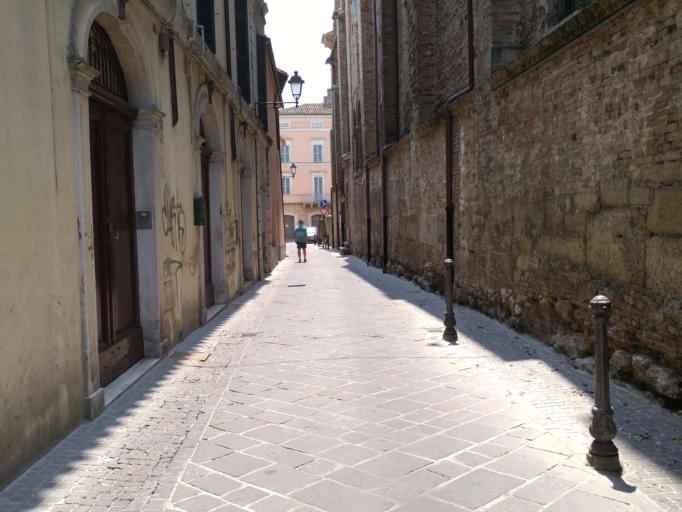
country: IT
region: Abruzzo
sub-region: Provincia di Teramo
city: Atri
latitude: 42.5805
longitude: 13.9769
